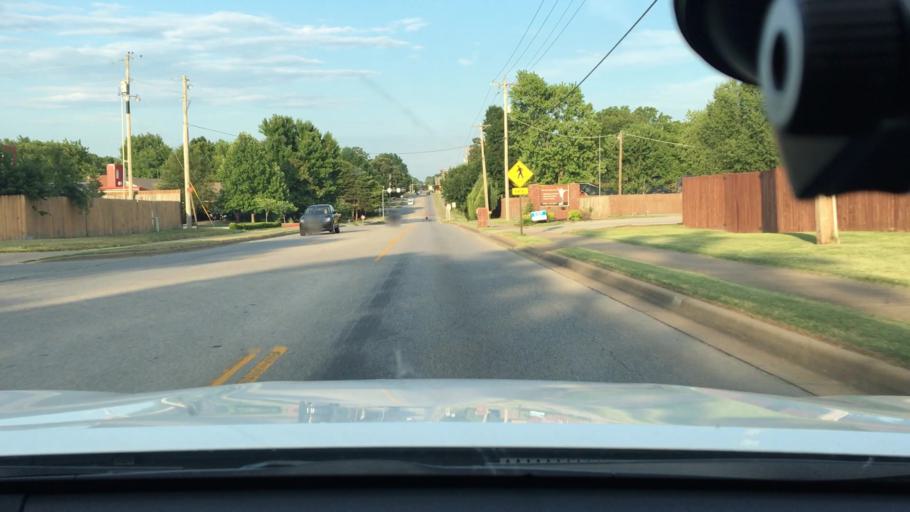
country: US
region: Arkansas
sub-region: Benton County
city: Rogers
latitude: 36.3417
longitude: -94.1603
